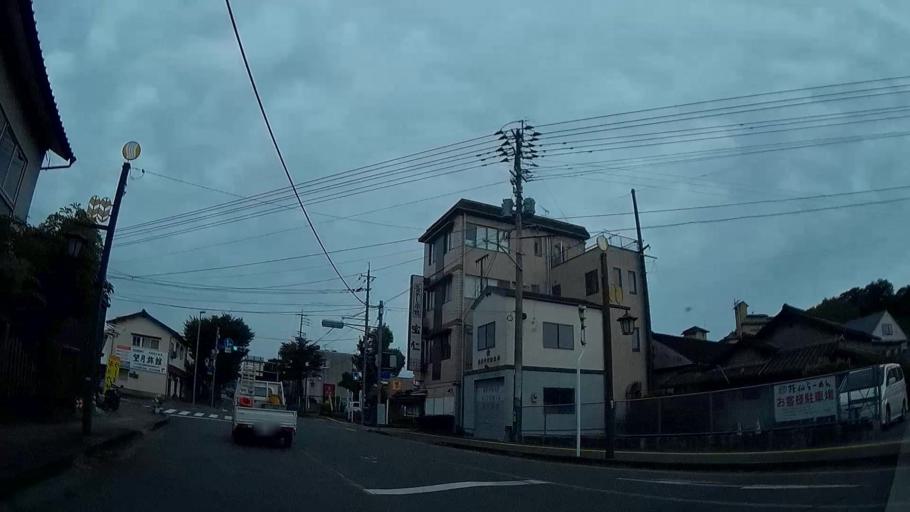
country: JP
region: Kumamoto
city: Kikuchi
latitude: 32.9825
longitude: 130.8155
